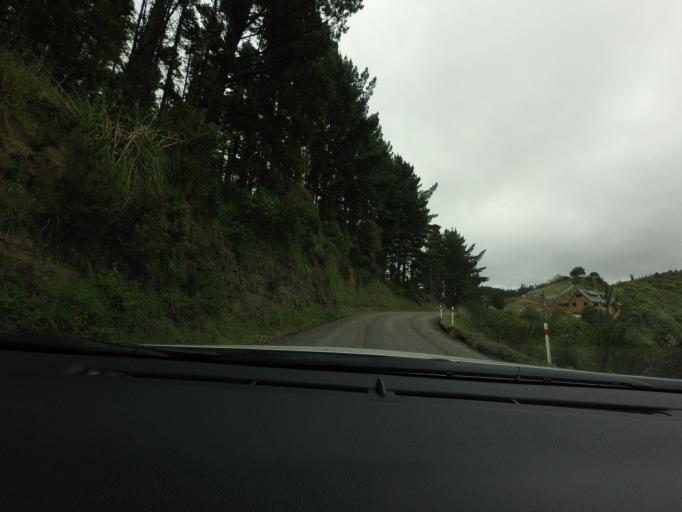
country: NZ
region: Auckland
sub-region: Auckland
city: Warkworth
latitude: -36.4858
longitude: 174.6073
